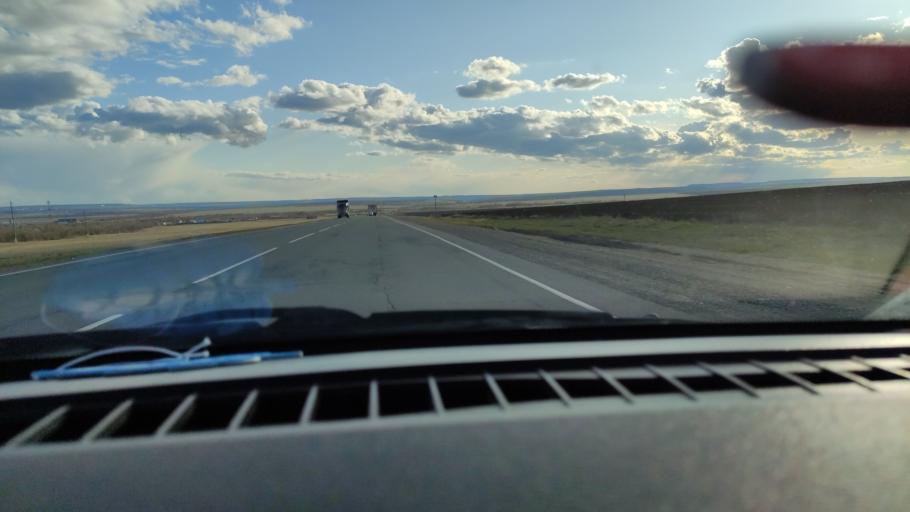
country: RU
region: Saratov
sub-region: Saratovskiy Rayon
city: Saratov
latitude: 51.7418
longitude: 46.0462
